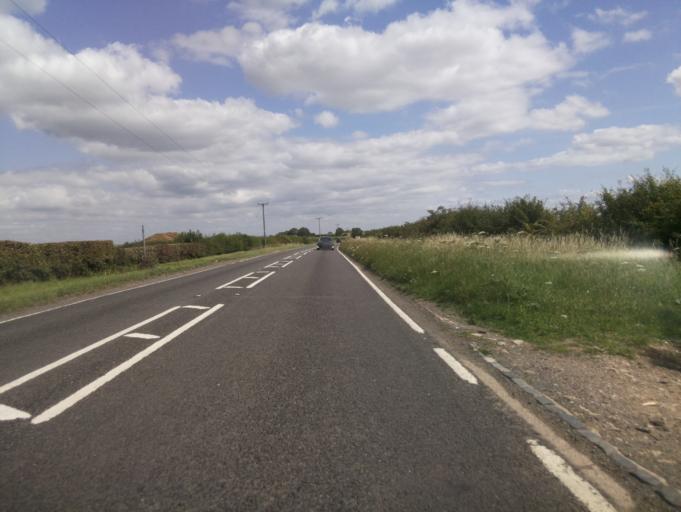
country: GB
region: England
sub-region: Buckinghamshire
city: Winslow
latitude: 51.8888
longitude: -0.8376
